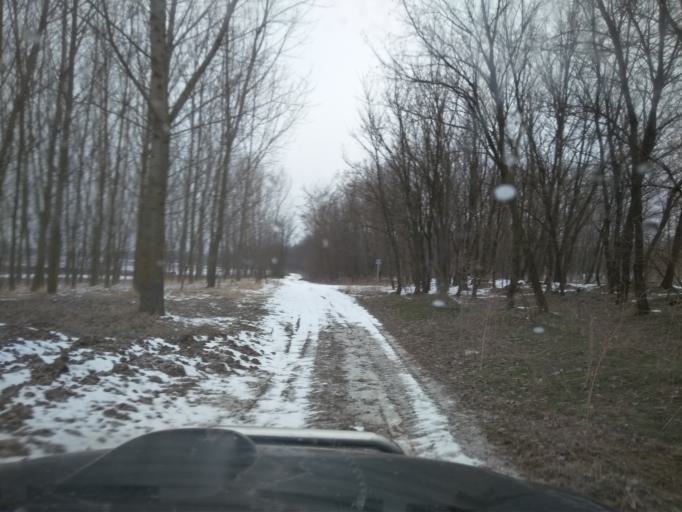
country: HU
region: Szabolcs-Szatmar-Bereg
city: Apagy
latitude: 47.9794
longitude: 21.9131
